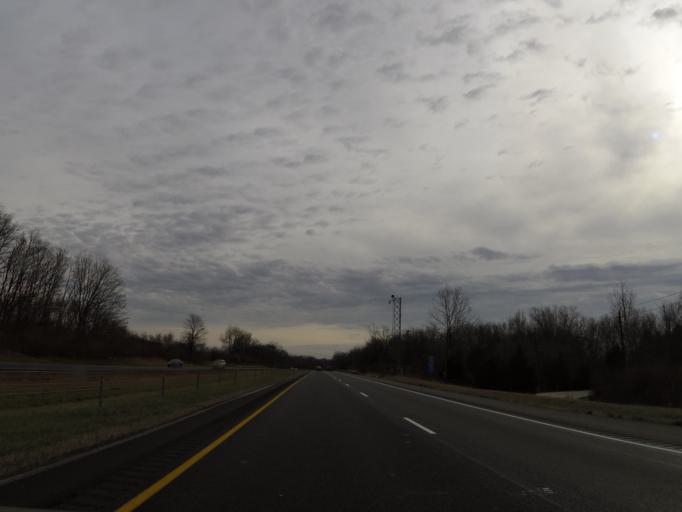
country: US
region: Indiana
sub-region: Marion County
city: Clermont
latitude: 39.8296
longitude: -86.3235
